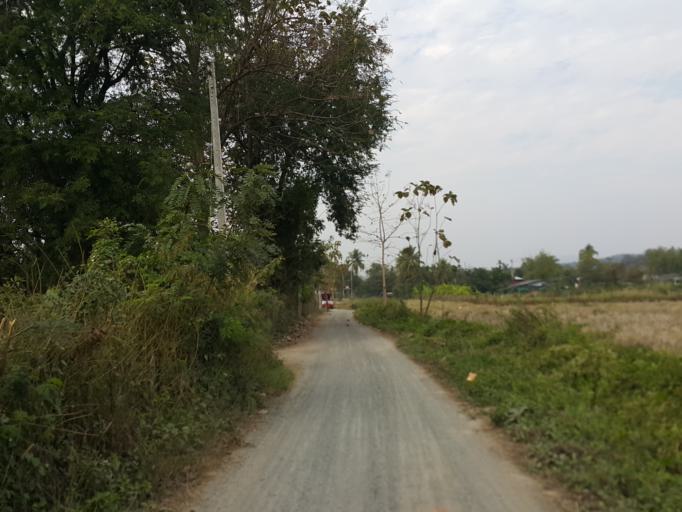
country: TH
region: Chiang Mai
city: San Kamphaeng
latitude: 18.8337
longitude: 99.1519
